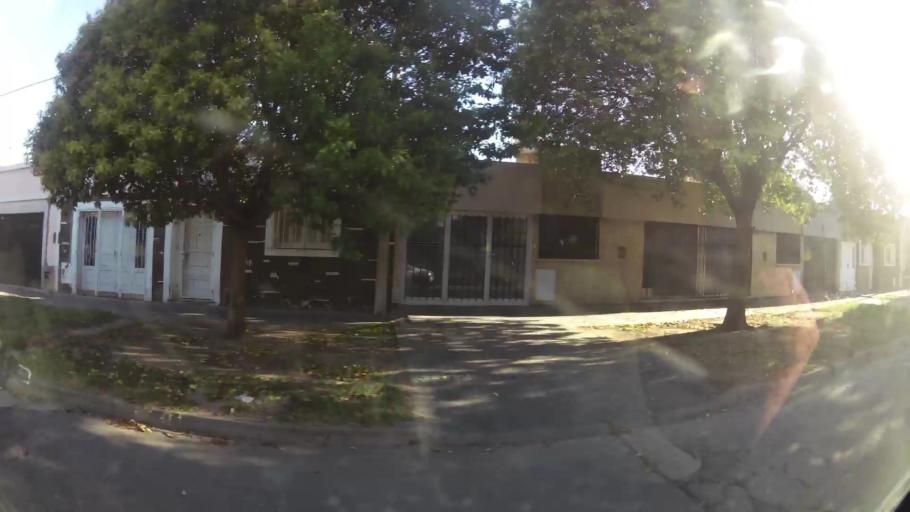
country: AR
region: Cordoba
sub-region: Departamento de Capital
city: Cordoba
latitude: -31.3794
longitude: -64.1830
